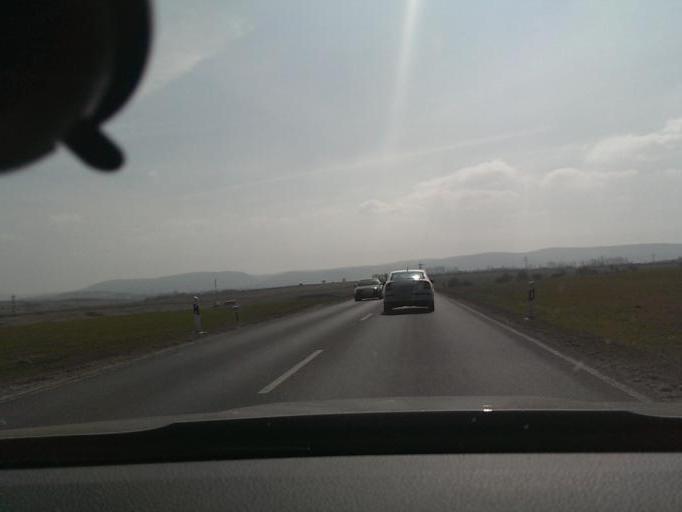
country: DE
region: Thuringia
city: Schwabhausen
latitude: 50.8794
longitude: 10.7277
